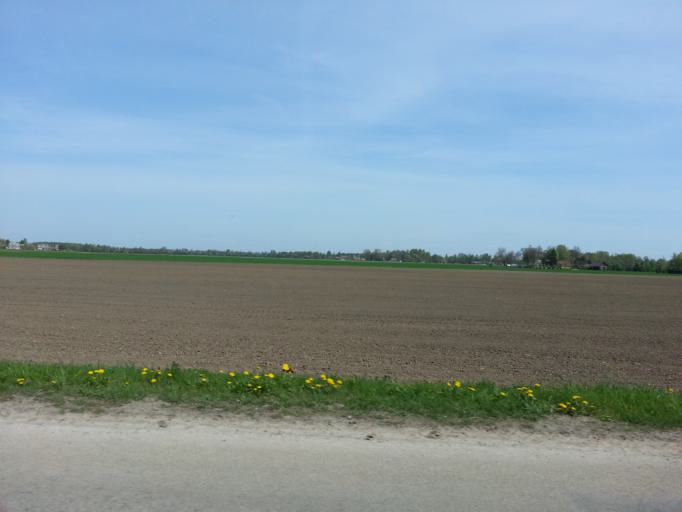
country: LT
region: Panevezys
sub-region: Panevezys City
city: Panevezys
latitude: 55.8225
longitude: 24.2620
